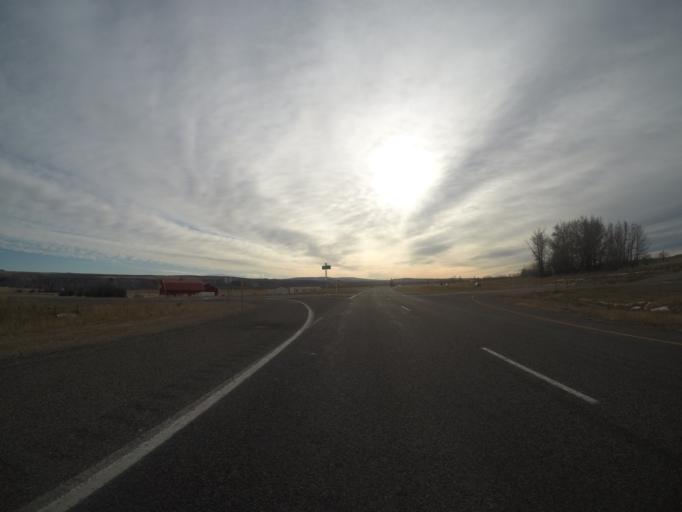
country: US
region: Montana
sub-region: Yellowstone County
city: Laurel
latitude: 45.5382
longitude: -108.8517
